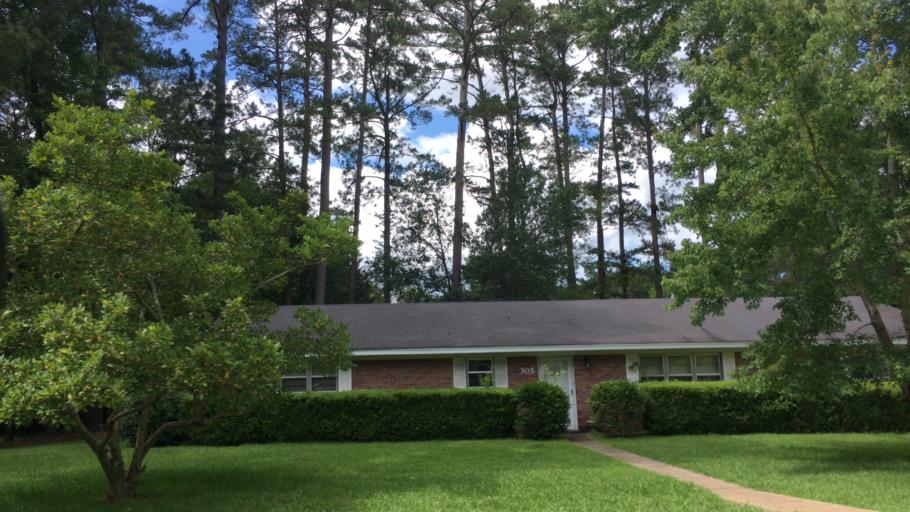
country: US
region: Louisiana
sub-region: Lincoln Parish
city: Ruston
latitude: 32.5480
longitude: -92.6361
